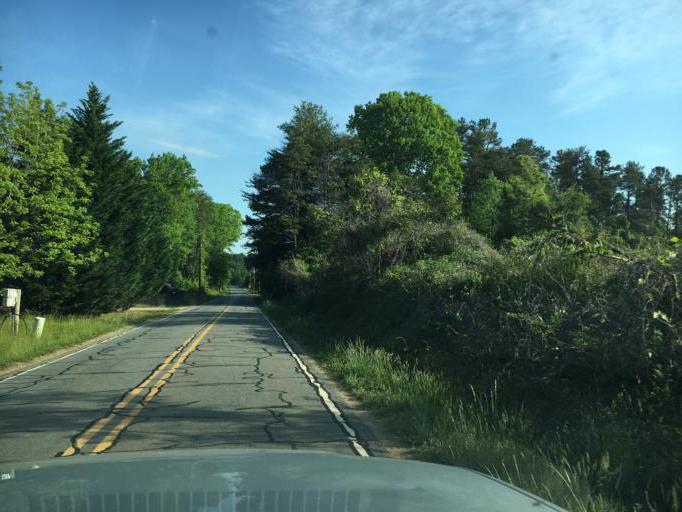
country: US
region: North Carolina
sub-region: Rutherford County
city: Rutherfordton
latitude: 35.3508
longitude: -81.9845
